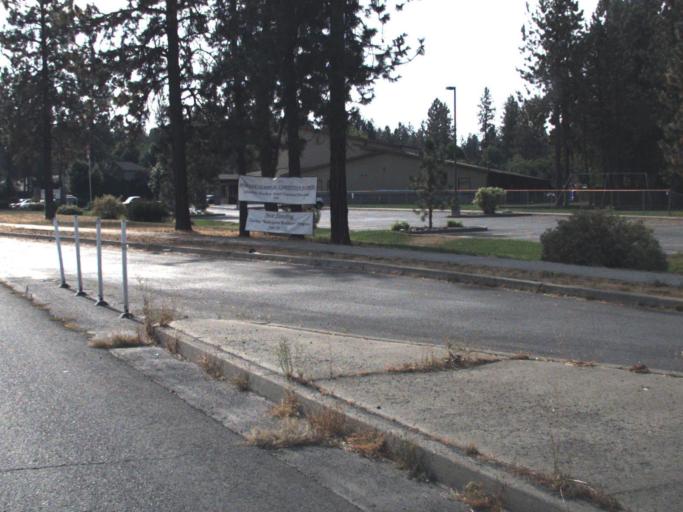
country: US
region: Washington
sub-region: Spokane County
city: Town and Country
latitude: 47.7242
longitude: -117.4931
